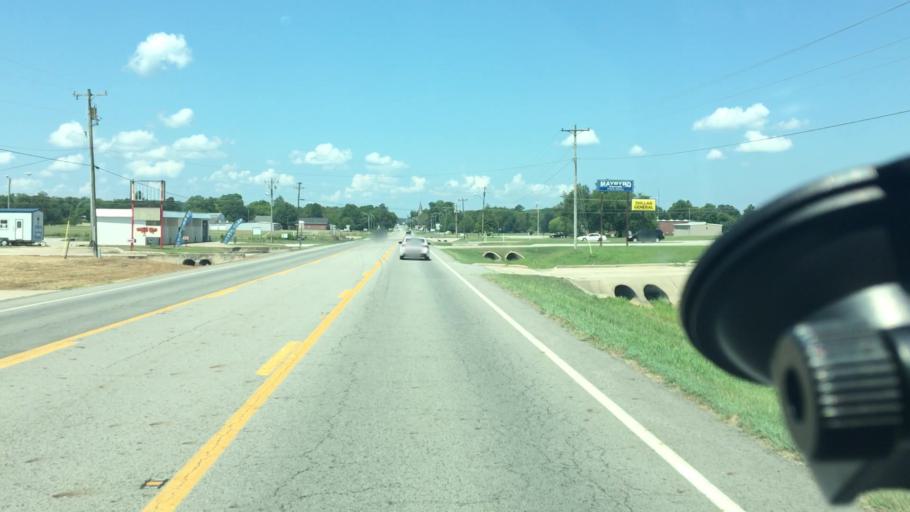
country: US
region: Arkansas
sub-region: Franklin County
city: Charleston
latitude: 35.2969
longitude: -94.0241
